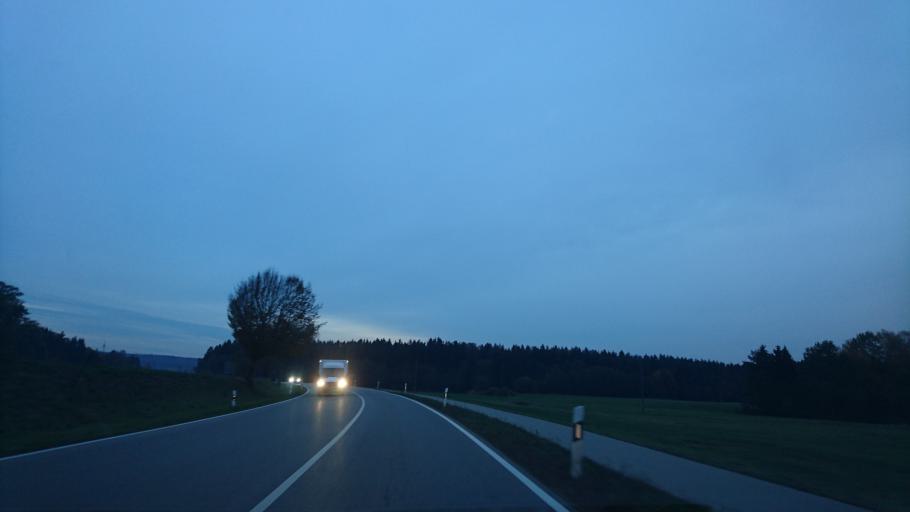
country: DE
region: Bavaria
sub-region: Swabia
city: Horgau
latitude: 48.3772
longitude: 10.7000
